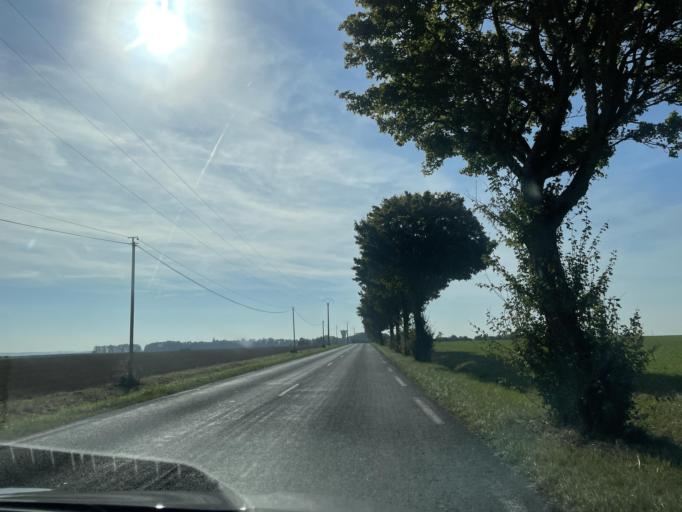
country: FR
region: Ile-de-France
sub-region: Departement de Seine-et-Marne
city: Coulommiers
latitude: 48.8551
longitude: 3.0906
